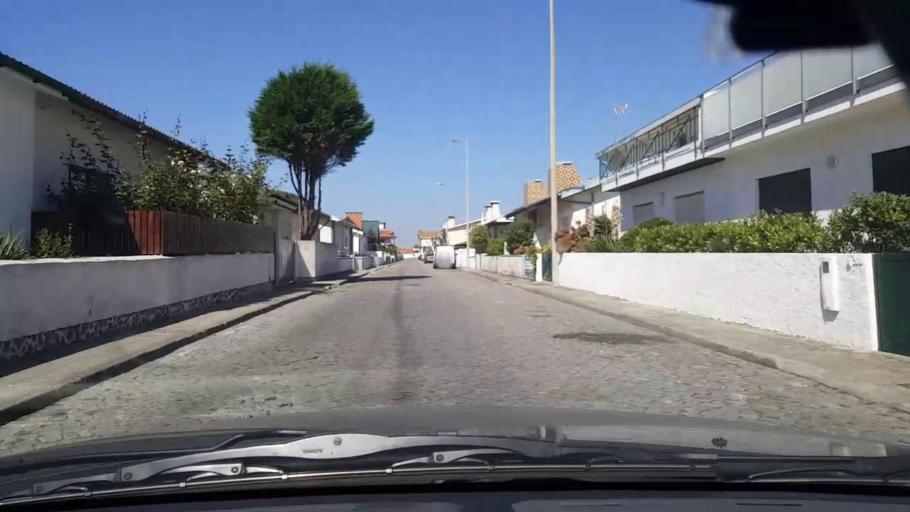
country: PT
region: Porto
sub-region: Vila do Conde
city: Arvore
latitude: 41.3080
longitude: -8.7354
